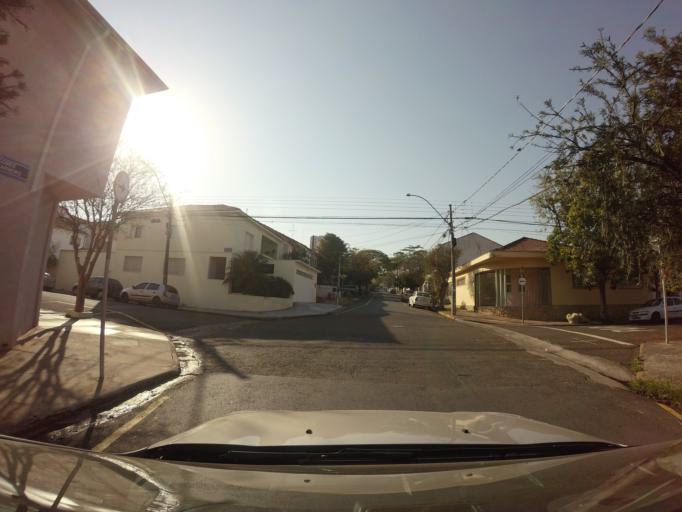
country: BR
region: Sao Paulo
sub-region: Piracicaba
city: Piracicaba
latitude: -22.7350
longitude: -47.6468
